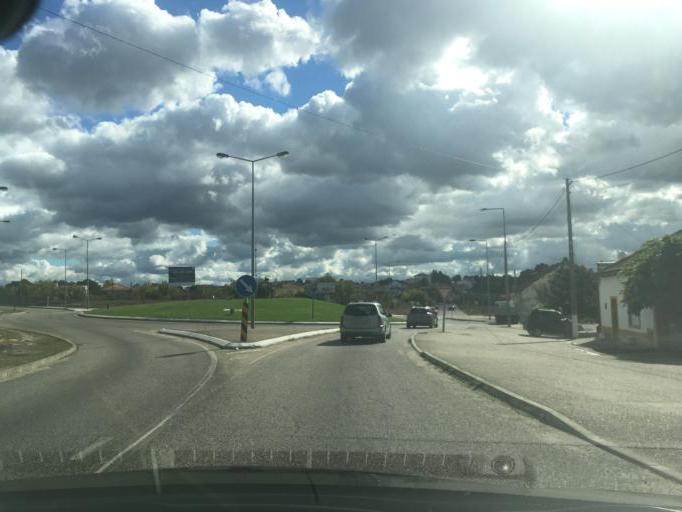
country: PT
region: Santarem
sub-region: Torres Novas
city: Riachos
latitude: 39.4521
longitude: -8.5188
